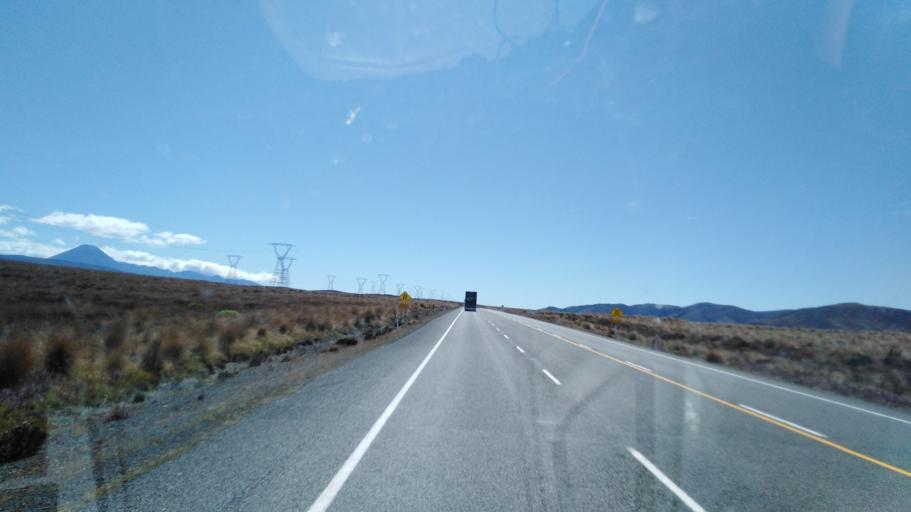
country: NZ
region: Manawatu-Wanganui
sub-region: Ruapehu District
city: Waiouru
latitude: -39.3688
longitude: 175.7138
